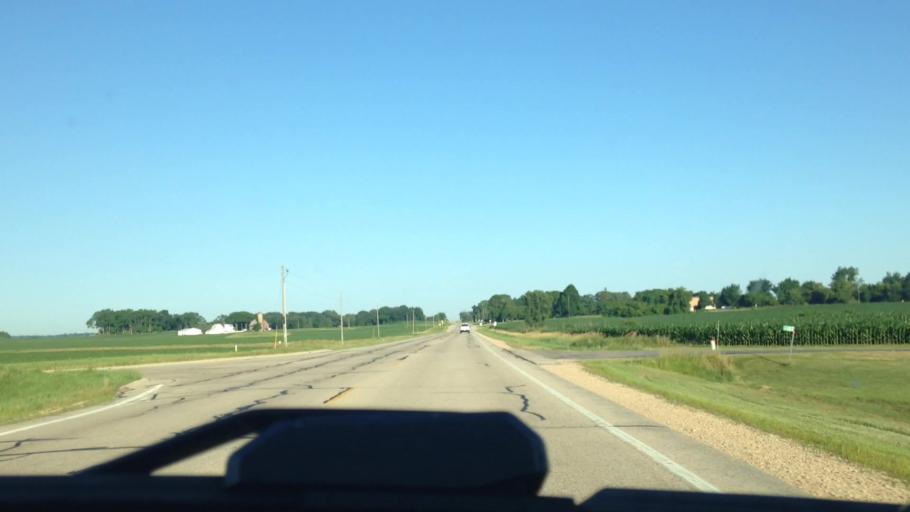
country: US
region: Wisconsin
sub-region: Columbia County
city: Fall River
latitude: 43.3403
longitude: -89.1661
